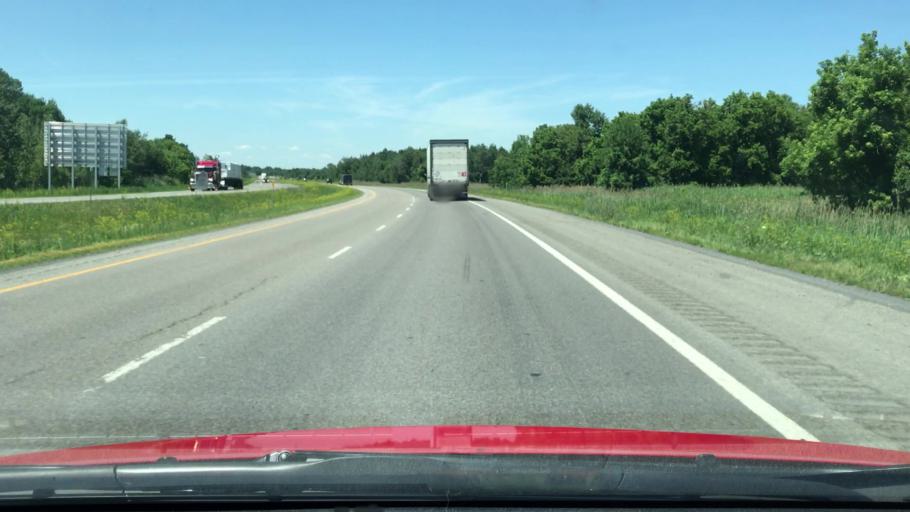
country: CA
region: Quebec
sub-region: Monteregie
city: Napierville
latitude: 45.1999
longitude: -73.4560
